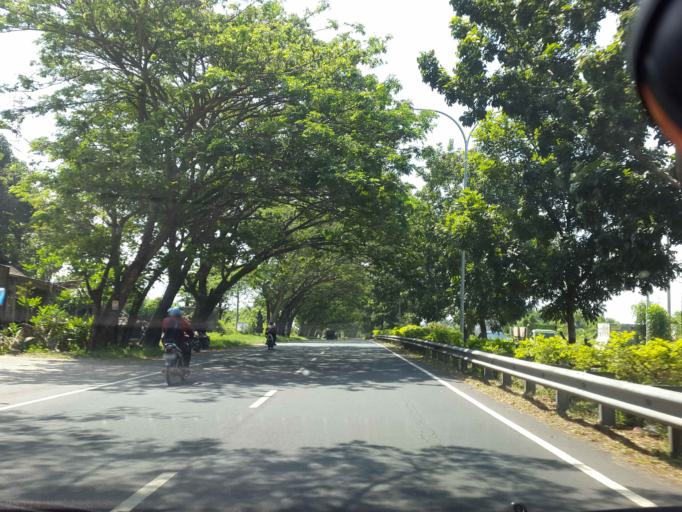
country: ID
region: Bali
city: Klungkung
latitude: -8.5681
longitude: 115.3755
